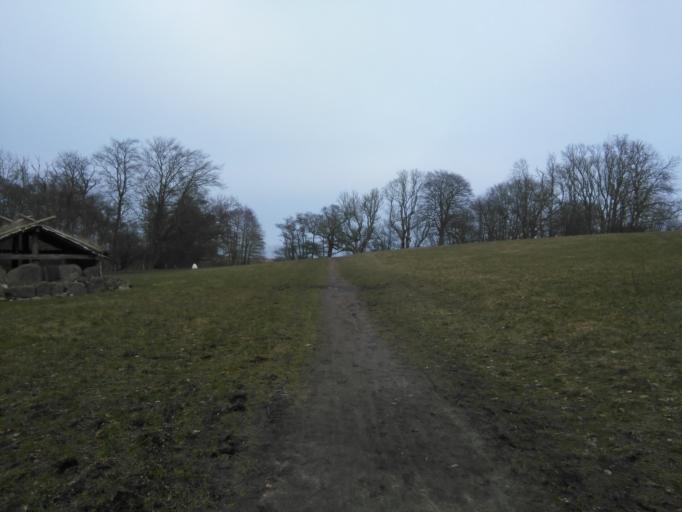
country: DK
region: Central Jutland
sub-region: Arhus Kommune
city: Beder
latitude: 56.0852
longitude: 10.2454
